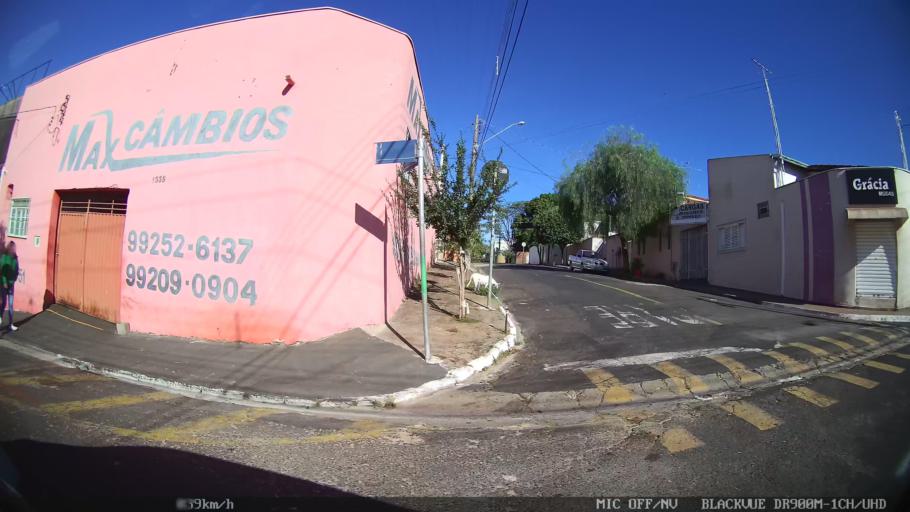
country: BR
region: Sao Paulo
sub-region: Franca
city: Franca
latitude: -20.5475
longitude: -47.4101
